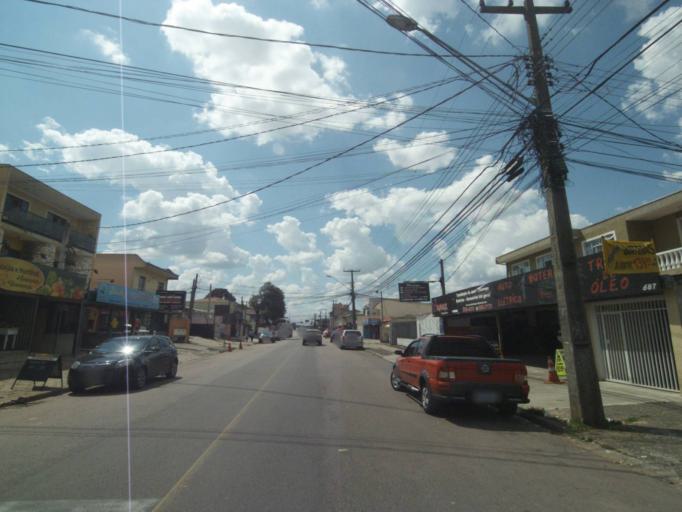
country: BR
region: Parana
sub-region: Sao Jose Dos Pinhais
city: Sao Jose dos Pinhais
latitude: -25.5383
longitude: -49.2721
